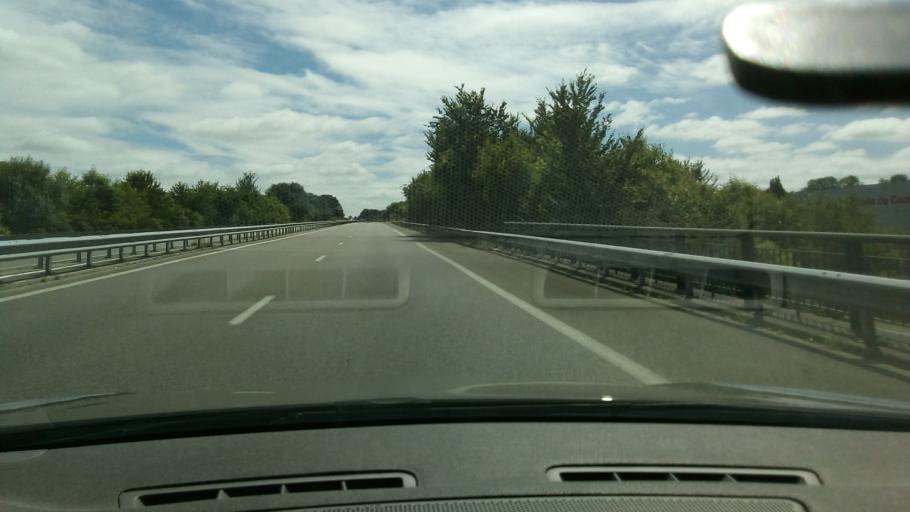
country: FR
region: Brittany
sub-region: Departement du Finistere
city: Ergue-Gaberic
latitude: 47.9781
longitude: -4.0325
